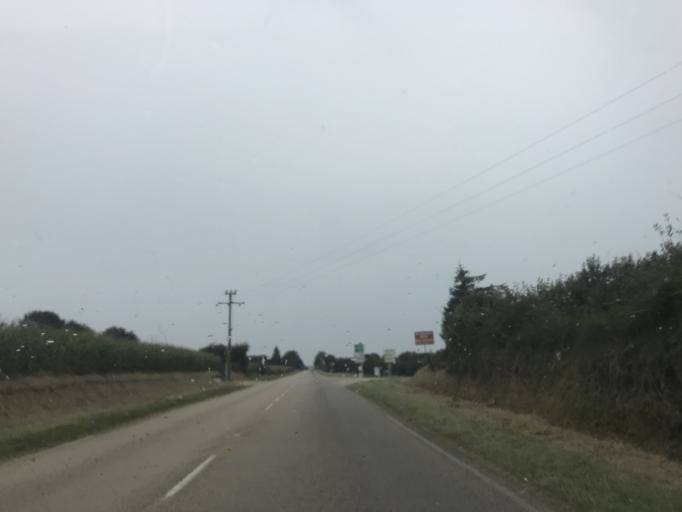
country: FR
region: Brittany
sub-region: Departement du Finistere
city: Plouneour-Menez
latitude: 48.4472
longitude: -3.8813
